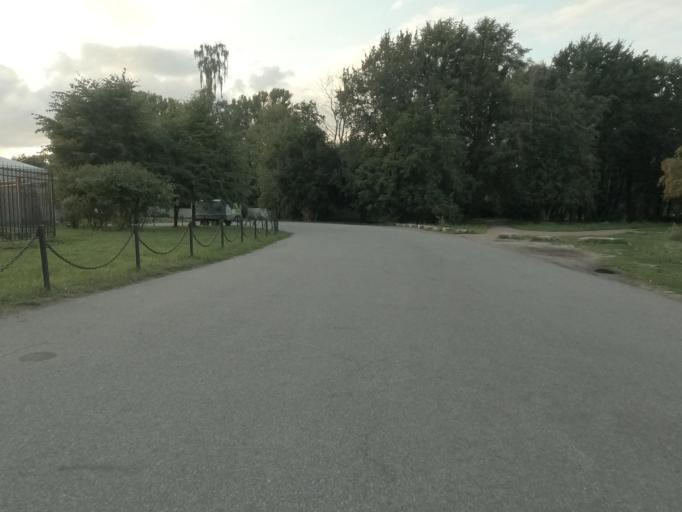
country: RU
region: St.-Petersburg
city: Admiralteisky
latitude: 59.8983
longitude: 30.2608
